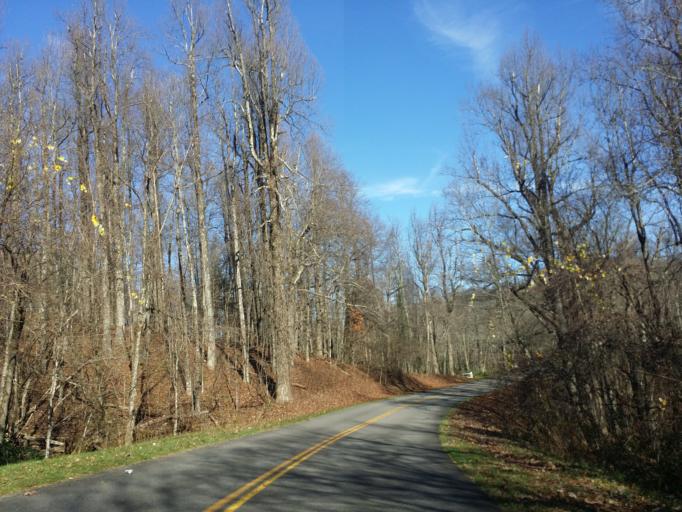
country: US
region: North Carolina
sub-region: Mitchell County
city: Spruce Pine
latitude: 35.8093
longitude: -82.1480
